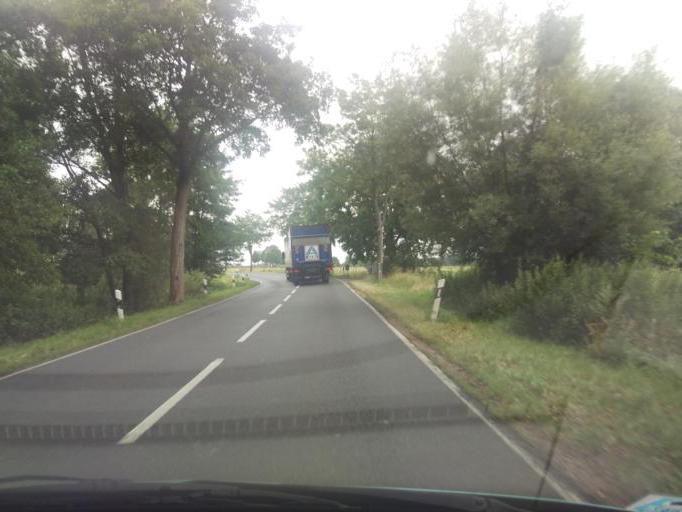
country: DE
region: Lower Saxony
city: Dollbergen
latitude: 52.3955
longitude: 10.1721
